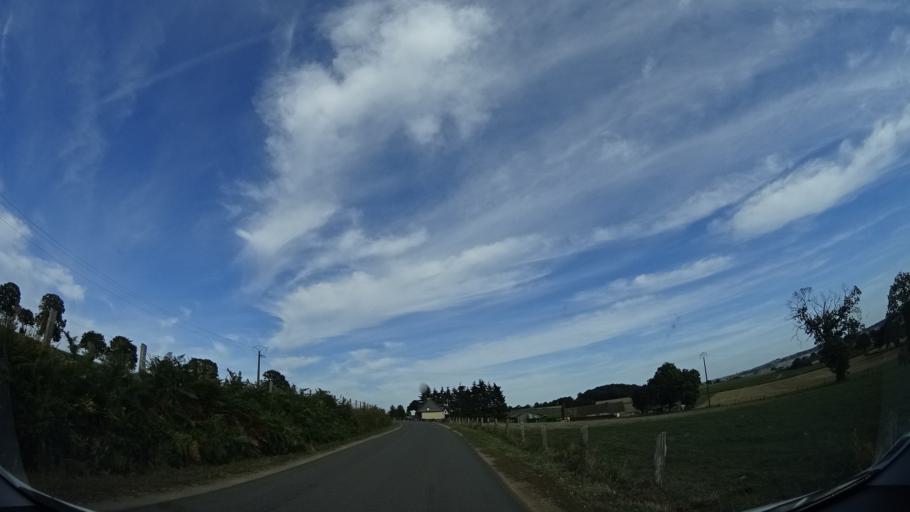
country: FR
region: Brittany
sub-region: Departement d'Ille-et-Vilaine
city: Romagne
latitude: 48.3326
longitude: -1.2537
